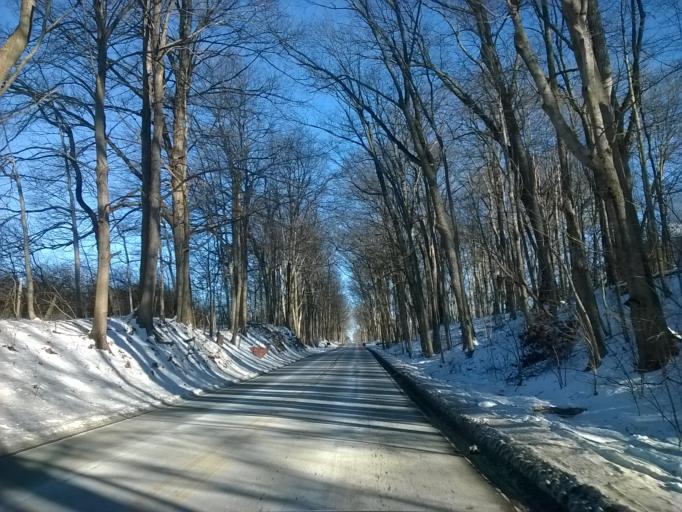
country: US
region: Indiana
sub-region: Boone County
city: Zionsville
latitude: 39.9247
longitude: -86.2770
